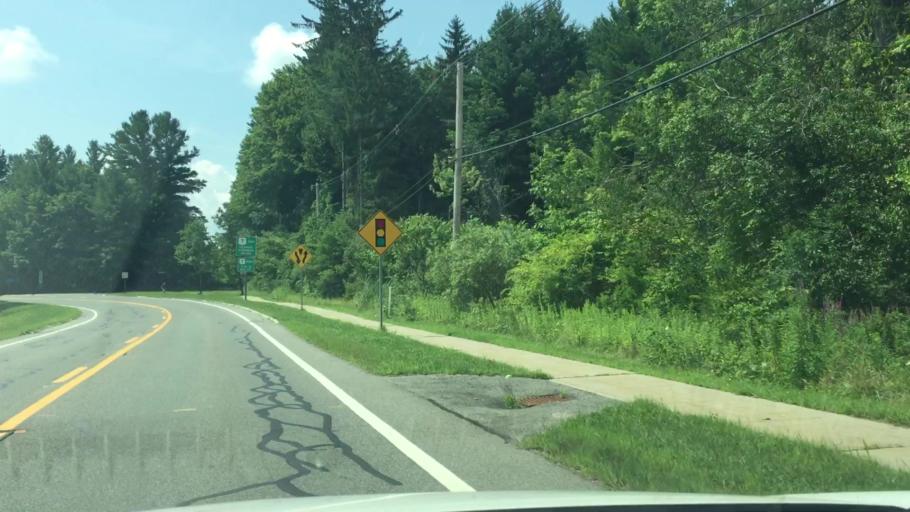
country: US
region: Massachusetts
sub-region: Berkshire County
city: Lenox
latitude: 42.3378
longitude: -73.2839
